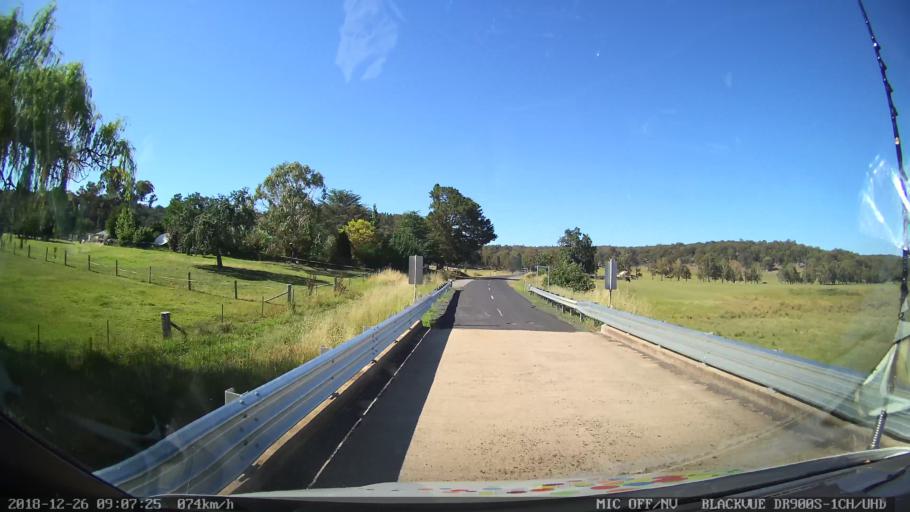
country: AU
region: New South Wales
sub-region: Mid-Western Regional
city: Kandos
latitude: -32.7053
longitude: 150.0044
